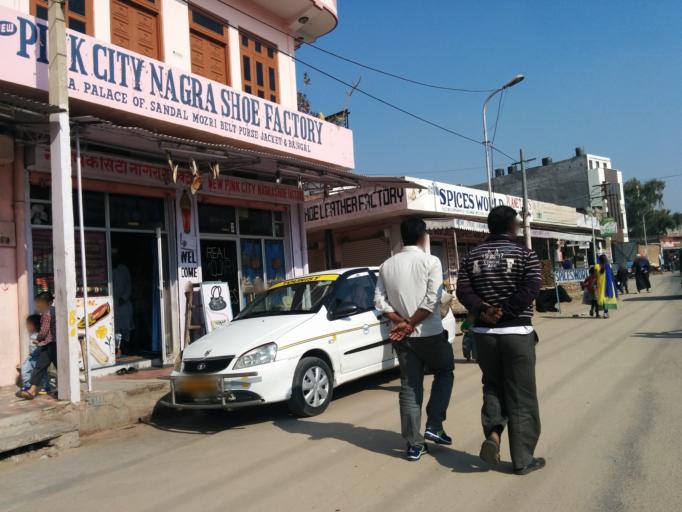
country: IN
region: Rajasthan
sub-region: Jaipur
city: Jaipur
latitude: 26.9461
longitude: 75.8385
